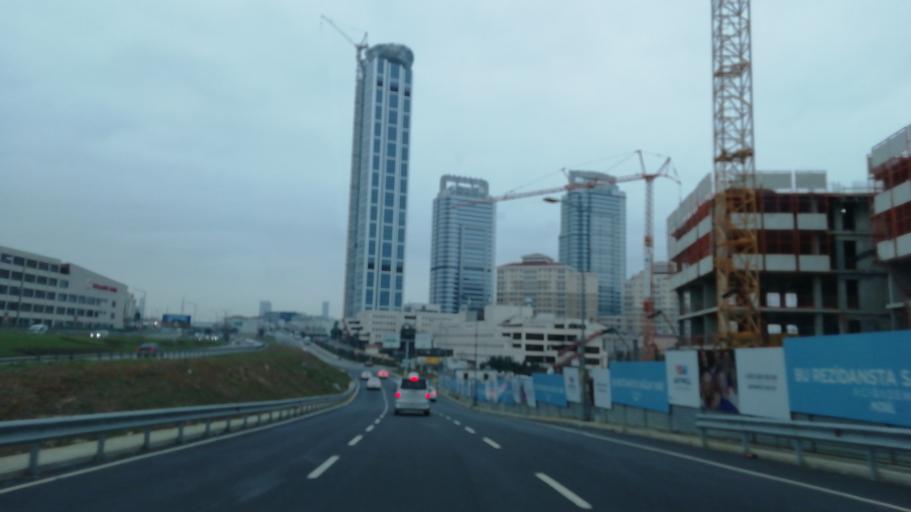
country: TR
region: Istanbul
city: UEskuedar
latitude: 41.0060
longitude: 29.0658
